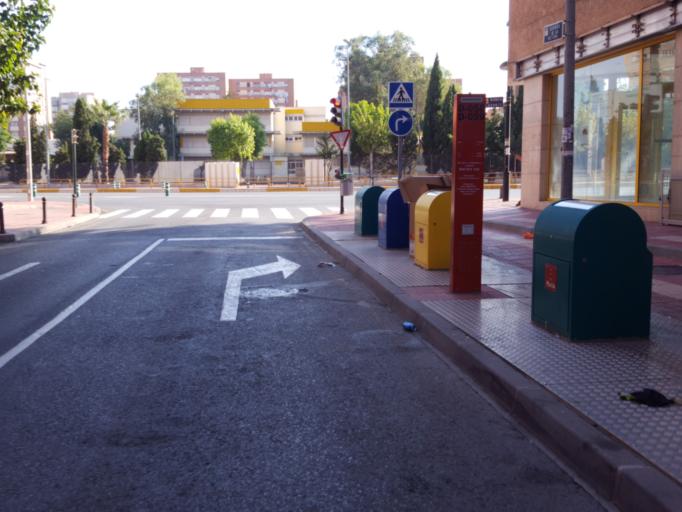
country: ES
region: Murcia
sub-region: Murcia
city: Murcia
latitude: 37.9915
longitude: -1.1218
